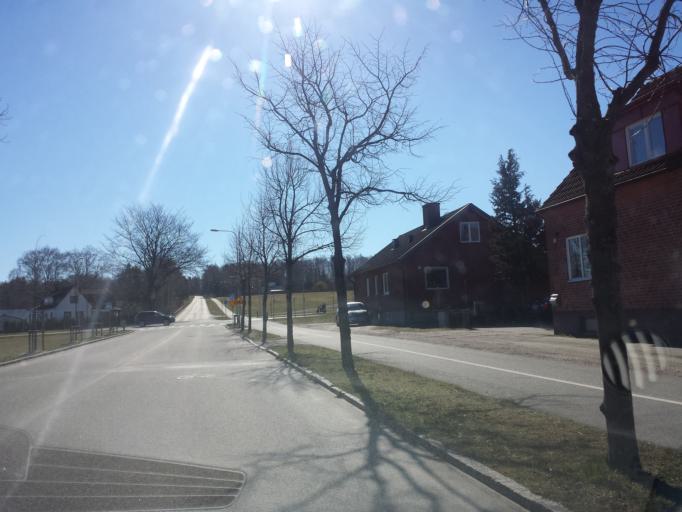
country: SE
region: Skane
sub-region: Sjobo Kommun
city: Sjoebo
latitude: 55.6291
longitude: 13.7111
